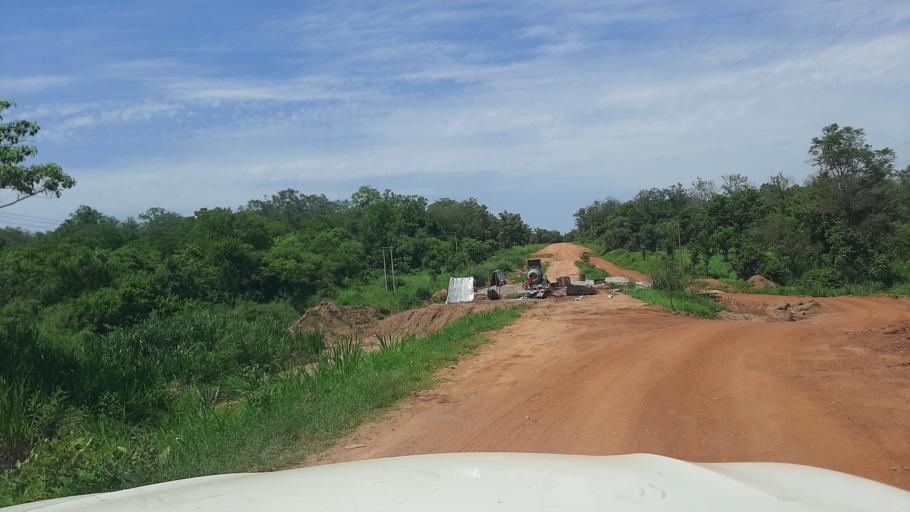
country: ET
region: Gambela
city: Gambela
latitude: 8.0893
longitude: 34.5896
